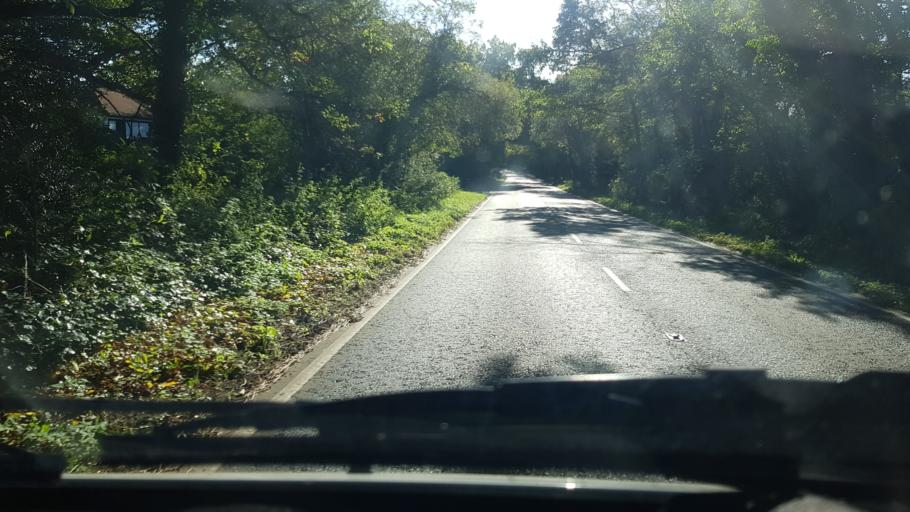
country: GB
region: England
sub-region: Surrey
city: Chilworth
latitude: 51.1778
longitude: -0.5207
